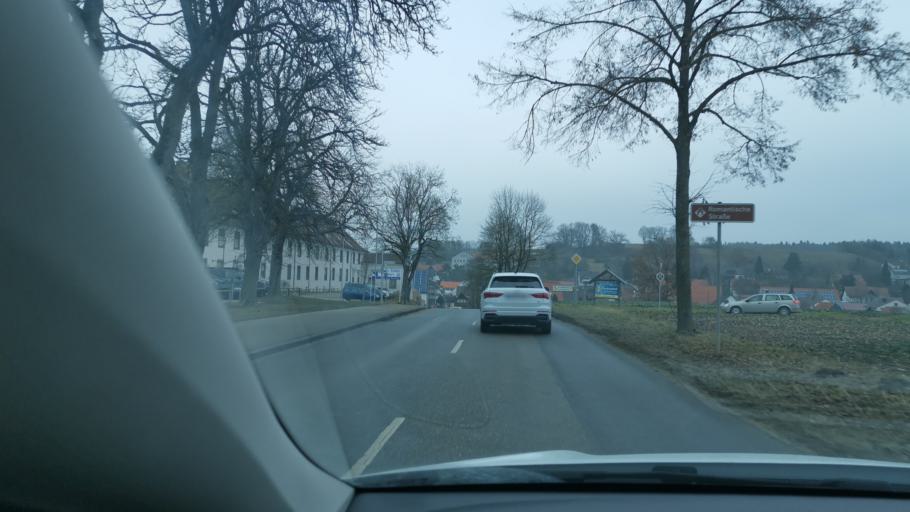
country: DE
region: Bavaria
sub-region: Swabia
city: Thierhaupten
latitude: 48.5605
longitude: 10.9120
